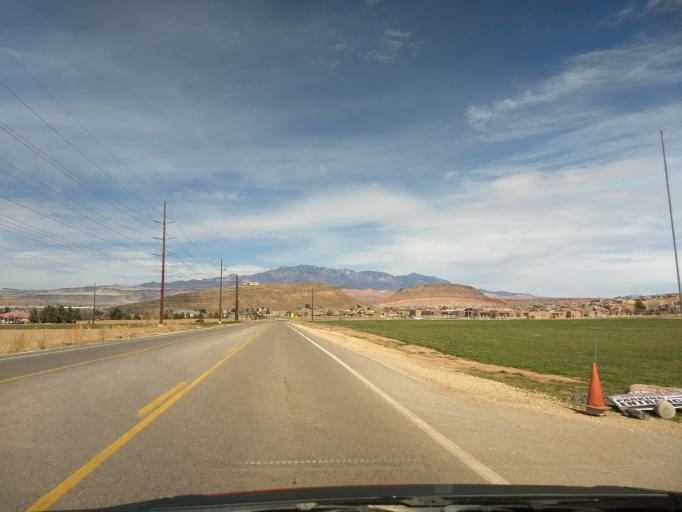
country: US
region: Utah
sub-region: Washington County
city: Washington
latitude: 37.0862
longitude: -113.4996
